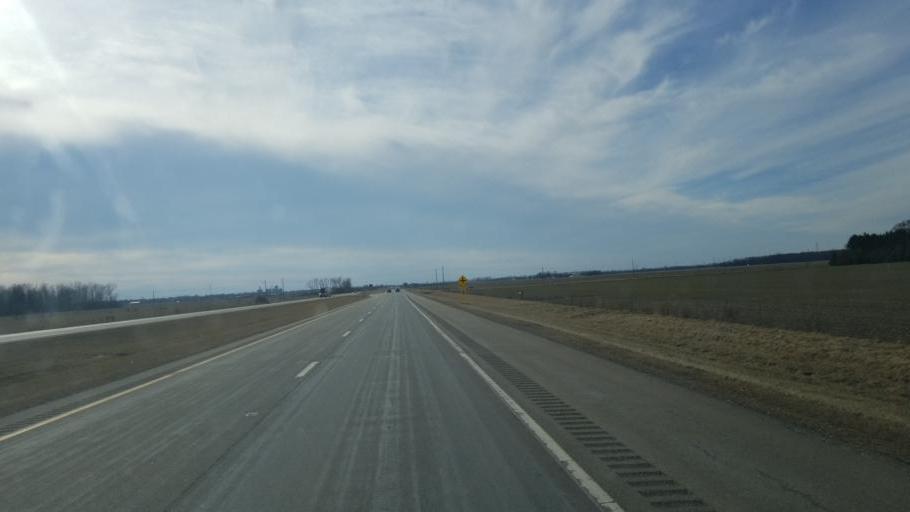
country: US
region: Ohio
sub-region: Van Wert County
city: Van Wert
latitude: 40.8852
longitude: -84.5394
